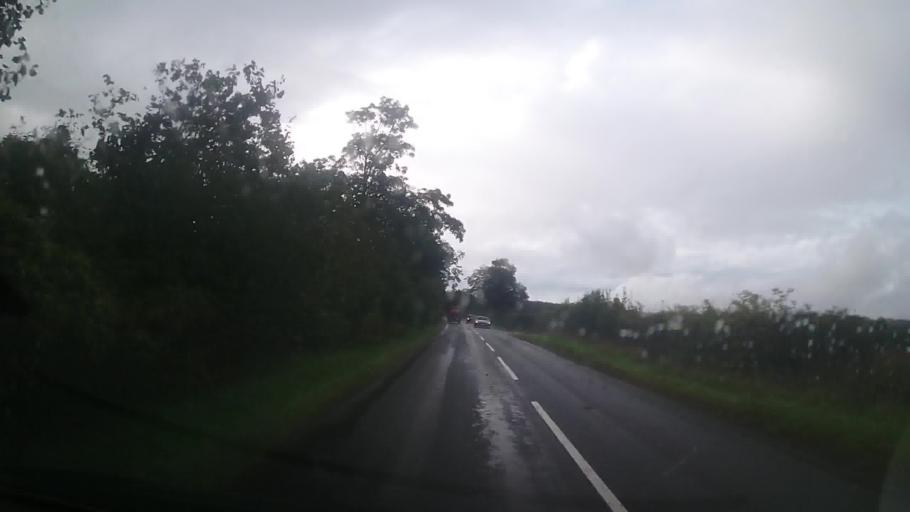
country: GB
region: England
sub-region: Oxfordshire
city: Stonesfield
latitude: 51.8707
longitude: -1.4153
